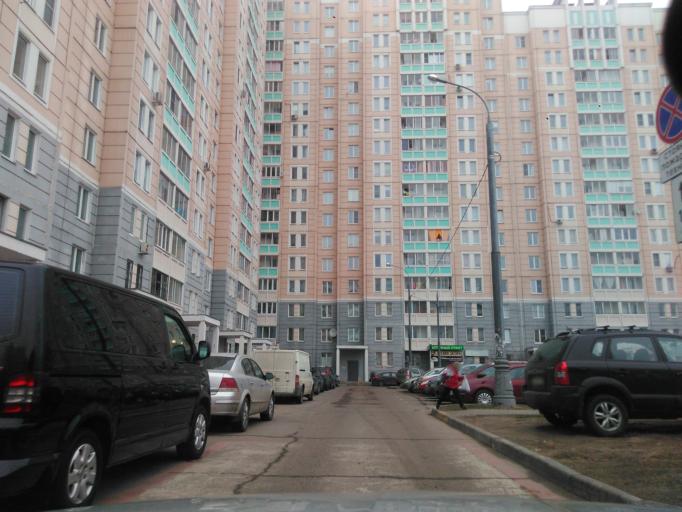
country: RU
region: Moscow
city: Zelenograd
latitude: 55.9738
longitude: 37.1654
